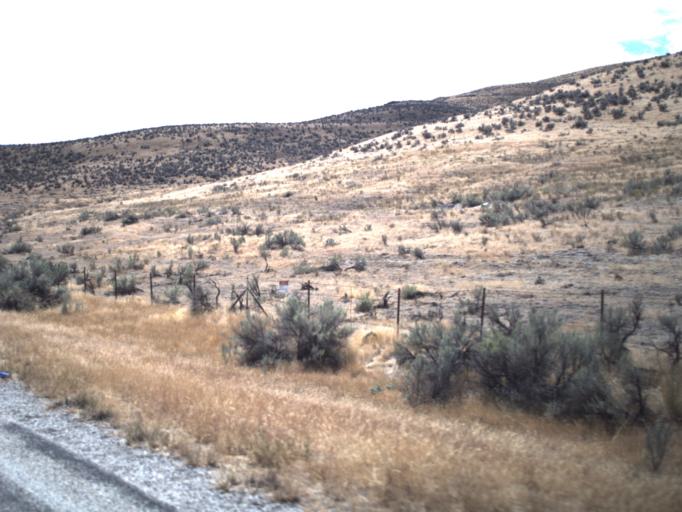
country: US
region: Utah
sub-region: Box Elder County
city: Tremonton
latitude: 41.6977
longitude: -112.4460
